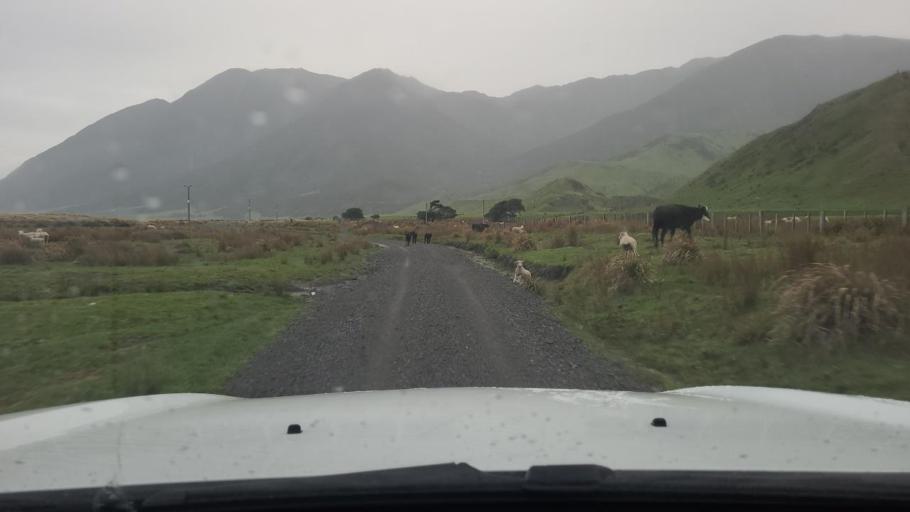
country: NZ
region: Wellington
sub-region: South Wairarapa District
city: Waipawa
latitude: -41.5666
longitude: 175.3849
